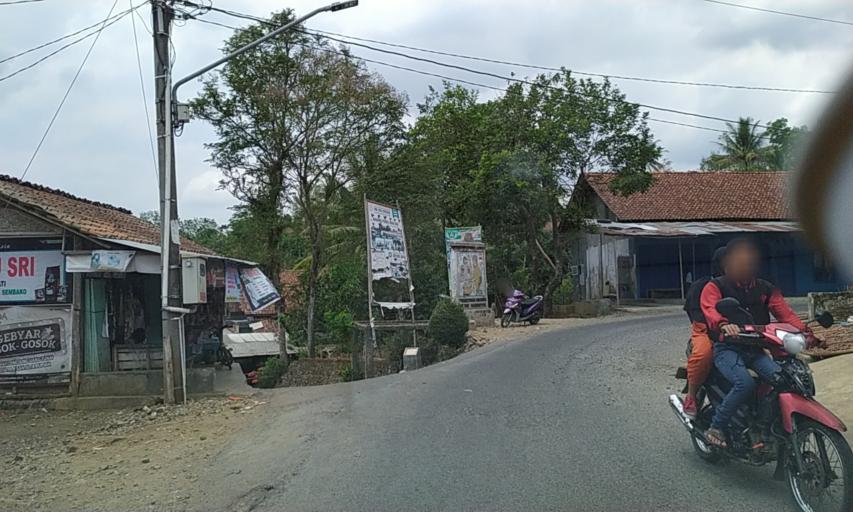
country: ID
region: Central Java
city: Telagasari
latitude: -7.3057
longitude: 108.8306
